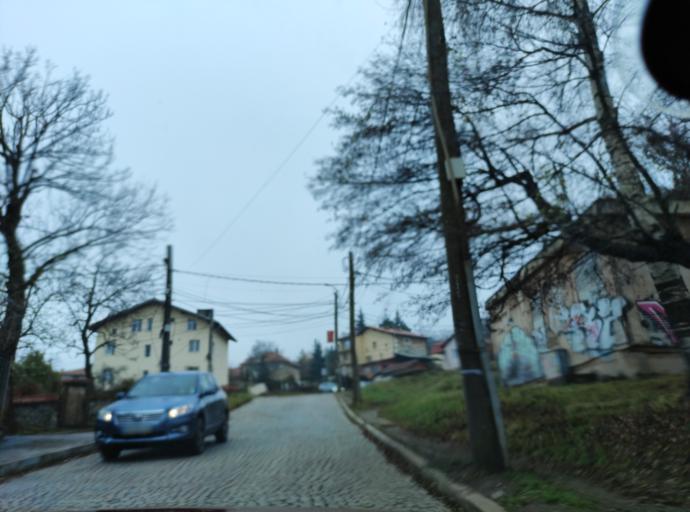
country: BG
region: Sofia-Capital
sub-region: Stolichna Obshtina
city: Sofia
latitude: 42.6263
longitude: 23.3079
